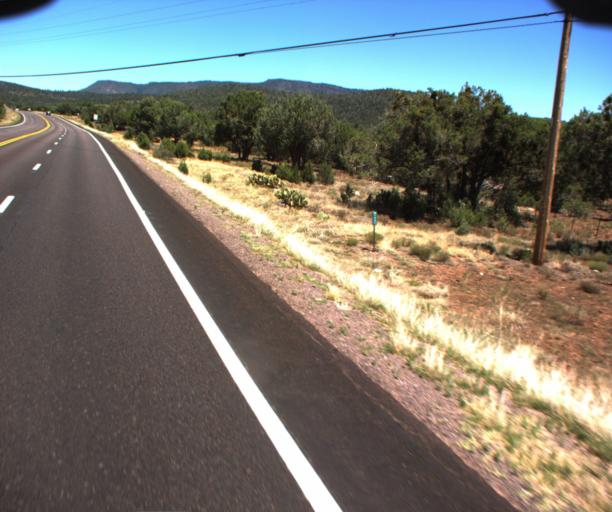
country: US
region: Arizona
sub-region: Gila County
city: Pine
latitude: 34.3269
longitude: -111.4180
